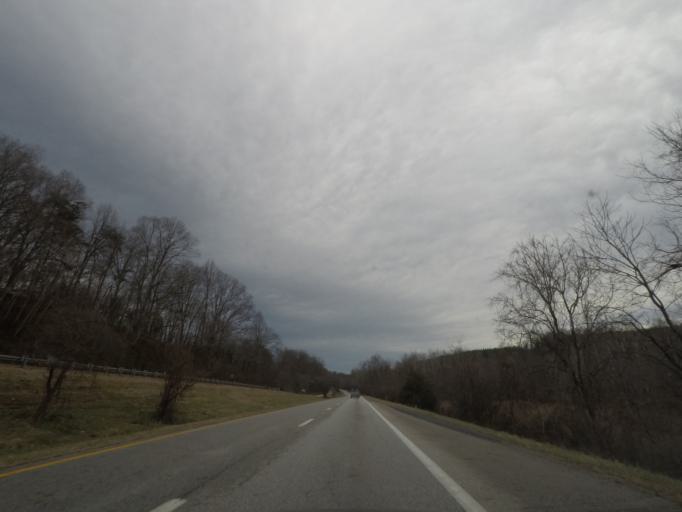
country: US
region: Virginia
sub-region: Nelson County
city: Lovingston
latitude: 37.8185
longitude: -78.8459
